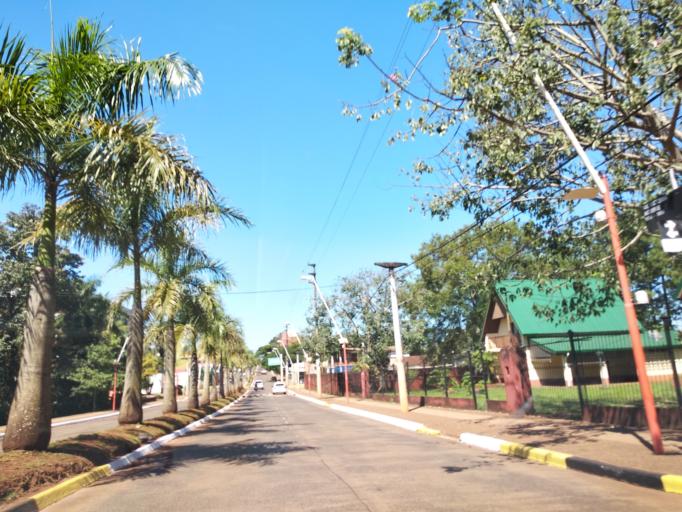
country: AR
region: Misiones
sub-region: Departamento de Iguazu
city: Puerto Iguazu
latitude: -25.6041
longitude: -54.5702
